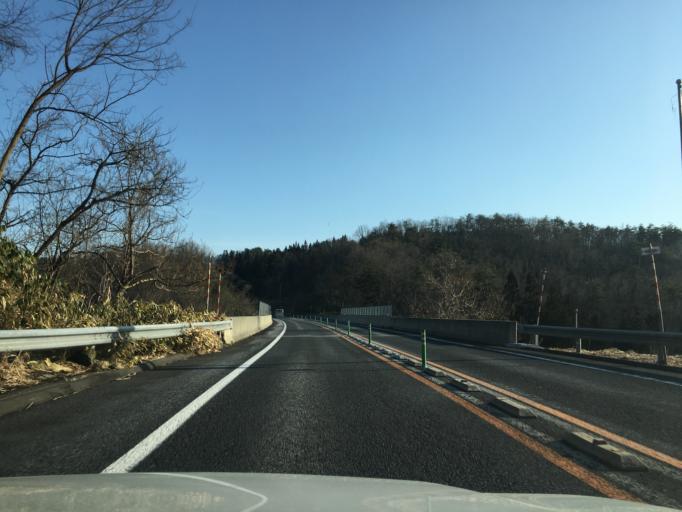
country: JP
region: Yamagata
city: Sagae
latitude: 38.4096
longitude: 140.1907
